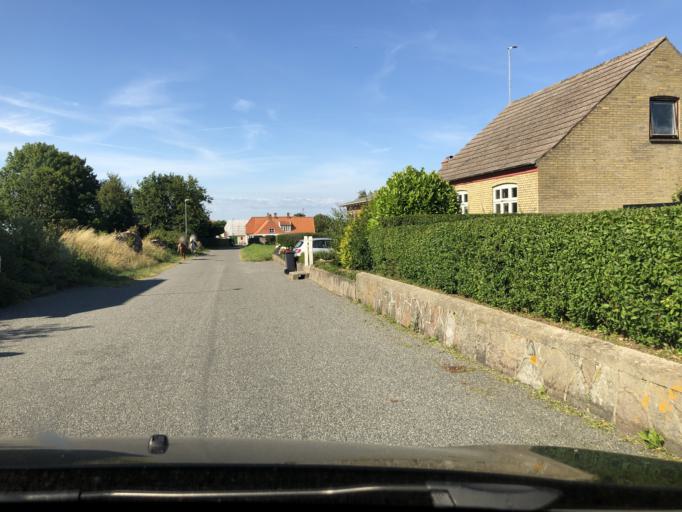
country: DK
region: South Denmark
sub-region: AEro Kommune
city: Marstal
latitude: 54.8731
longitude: 10.4897
